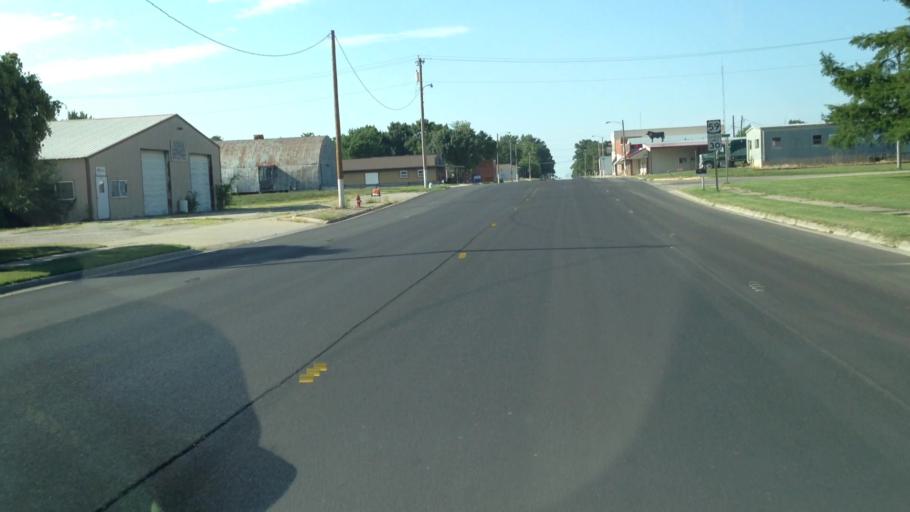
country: US
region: Kansas
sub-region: Allen County
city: Iola
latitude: 37.9135
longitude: -95.1701
